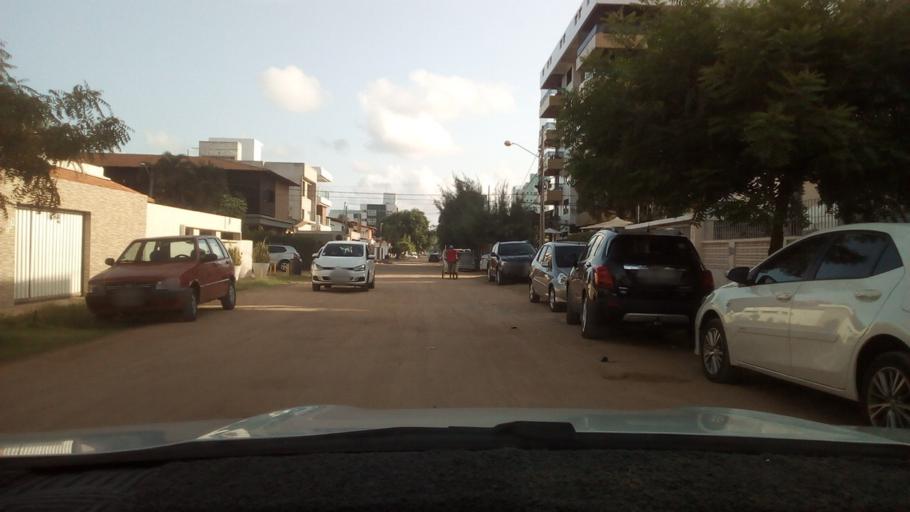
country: BR
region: Paraiba
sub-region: Cabedelo
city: Cabedelo
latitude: -7.0110
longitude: -34.8281
